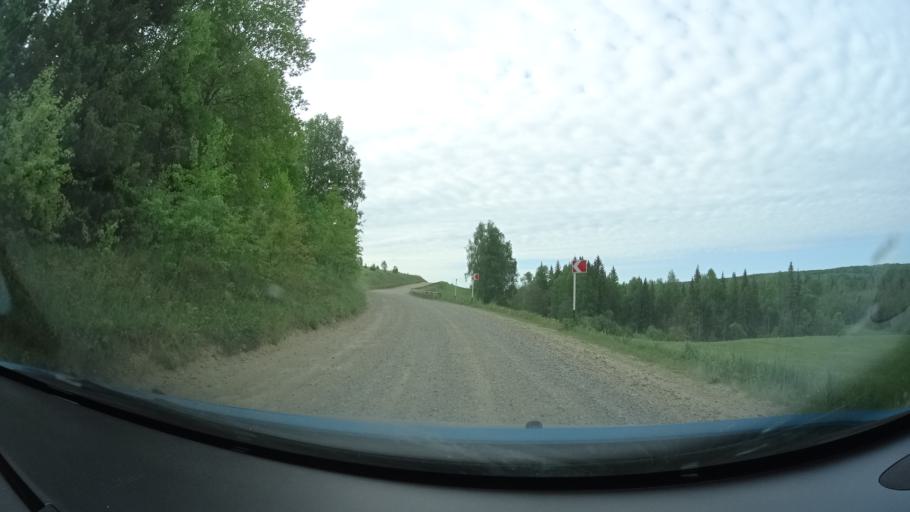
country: RU
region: Perm
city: Kuyeda
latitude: 56.6496
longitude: 55.6985
